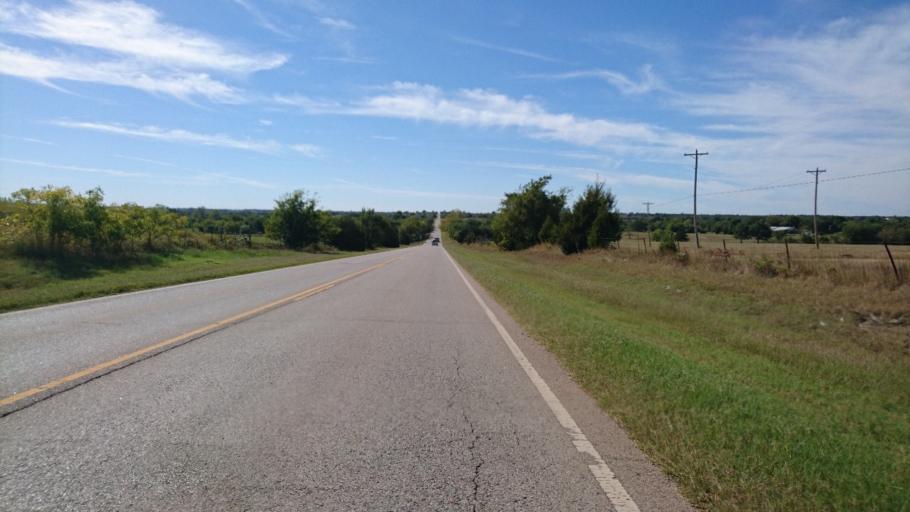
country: US
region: Oklahoma
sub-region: Lincoln County
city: Chandler
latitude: 35.7098
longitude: -96.7878
